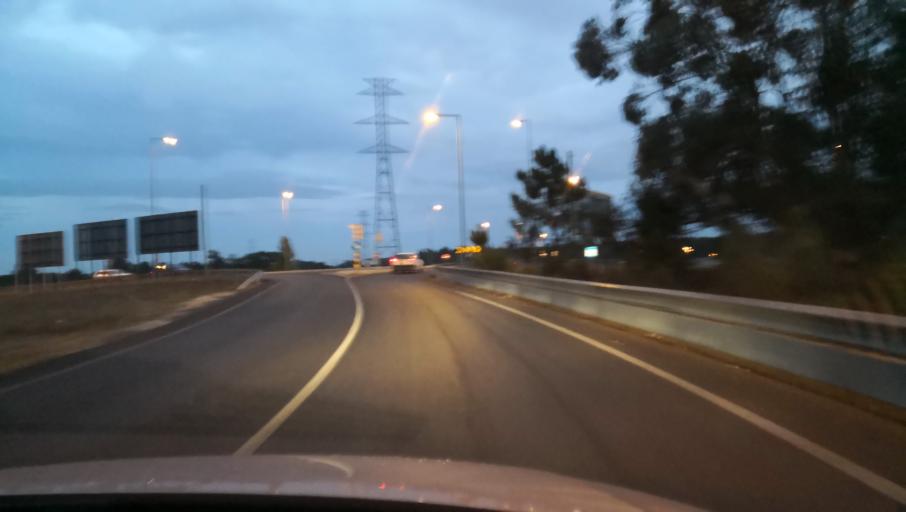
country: PT
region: Setubal
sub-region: Seixal
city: Amora
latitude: 38.6037
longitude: -9.1305
